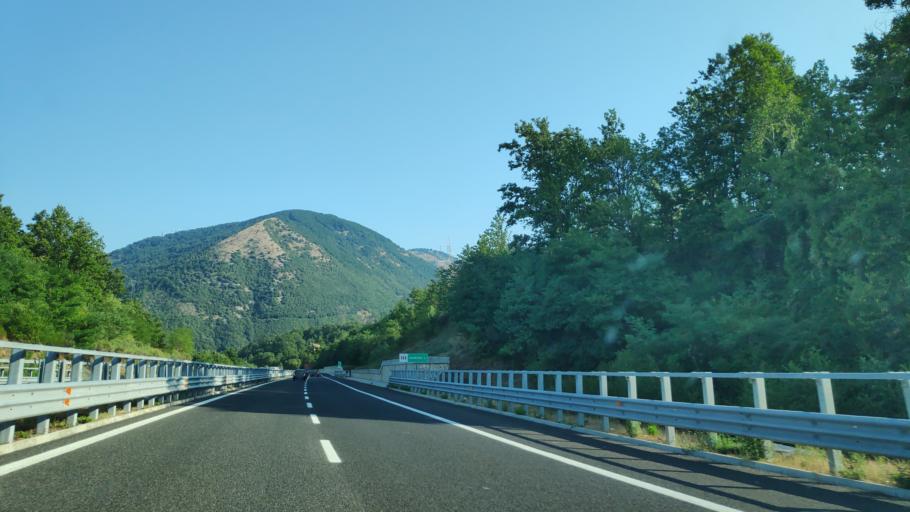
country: IT
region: Basilicate
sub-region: Provincia di Potenza
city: Lagonegro
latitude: 40.1175
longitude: 15.7847
